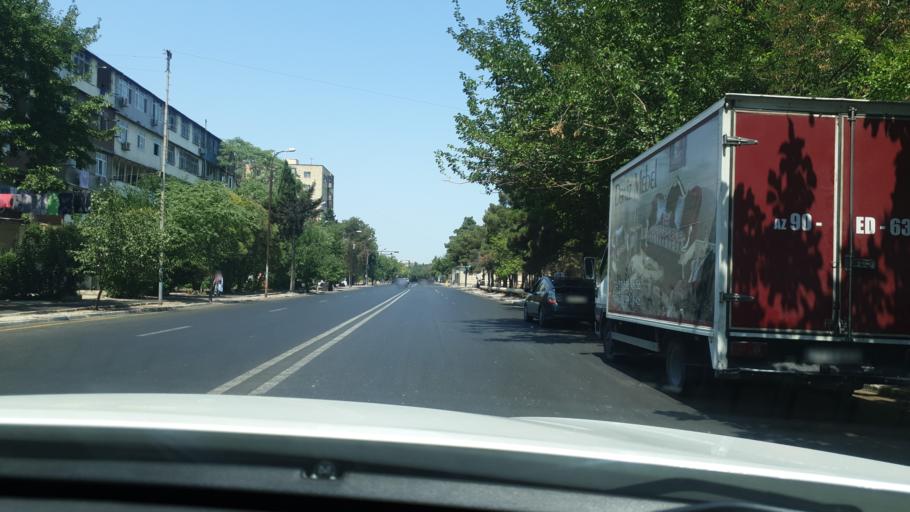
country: AZ
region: Baki
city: Bakixanov
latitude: 40.4156
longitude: 49.9476
